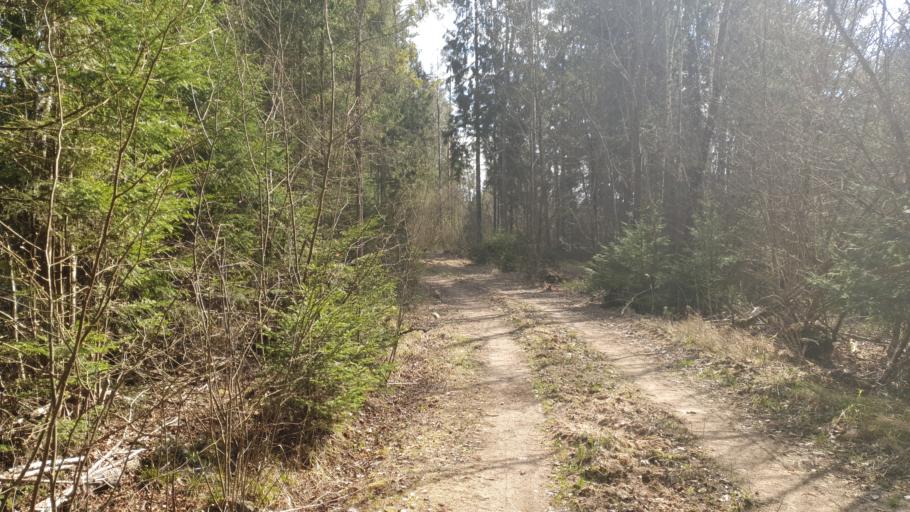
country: LT
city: Aukstadvaris
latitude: 54.4963
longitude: 24.6508
